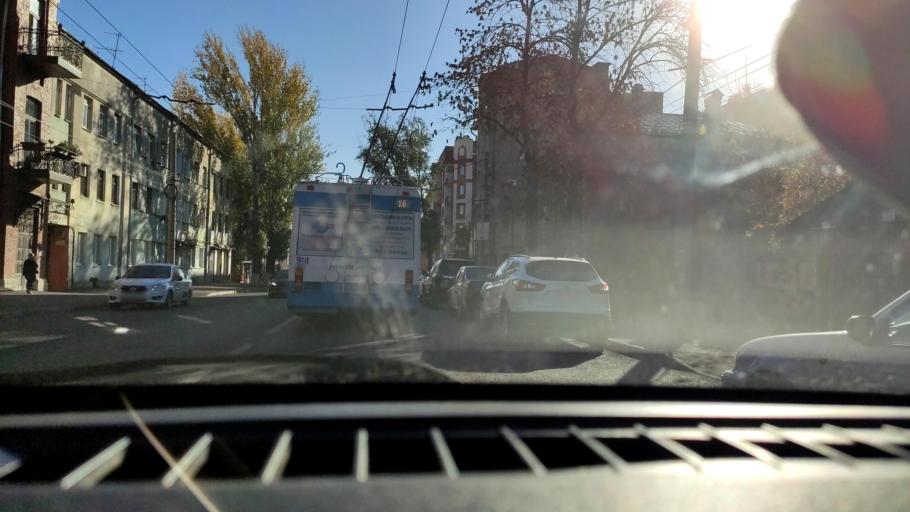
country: RU
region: Samara
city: Samara
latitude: 53.1895
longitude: 50.0941
